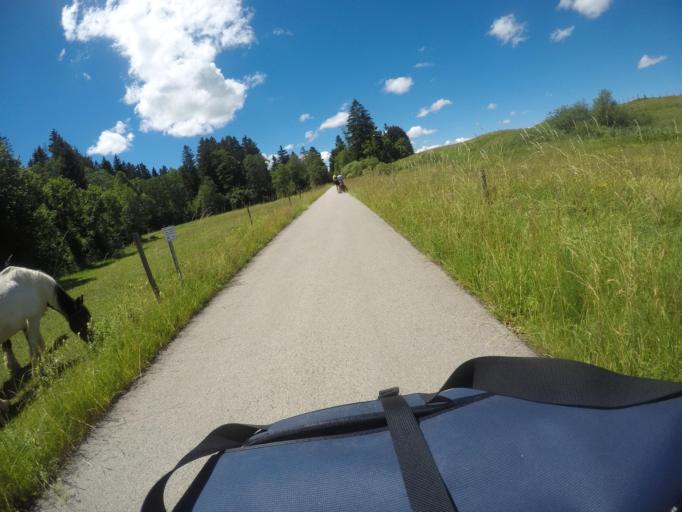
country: DE
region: Bavaria
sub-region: Swabia
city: Lechbruck
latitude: 47.6960
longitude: 10.7855
